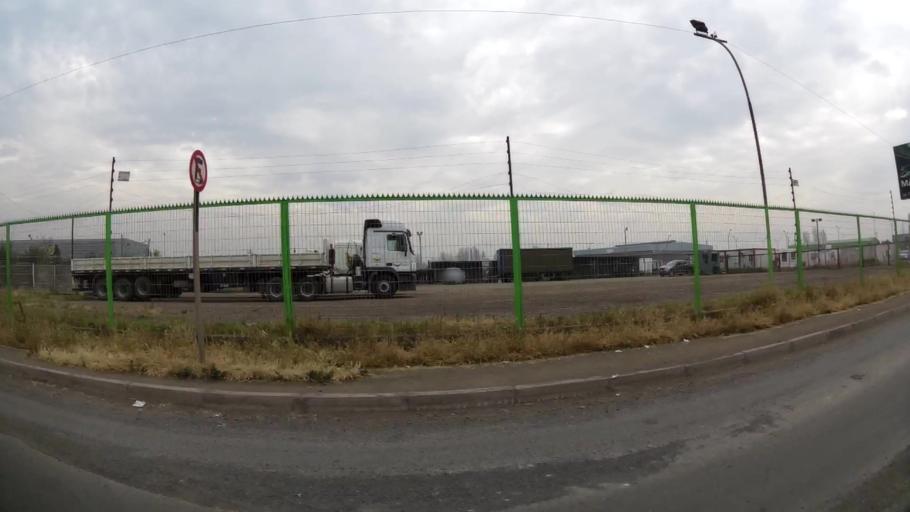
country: CL
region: Santiago Metropolitan
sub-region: Provincia de Chacabuco
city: Chicureo Abajo
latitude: -33.2663
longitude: -70.7456
